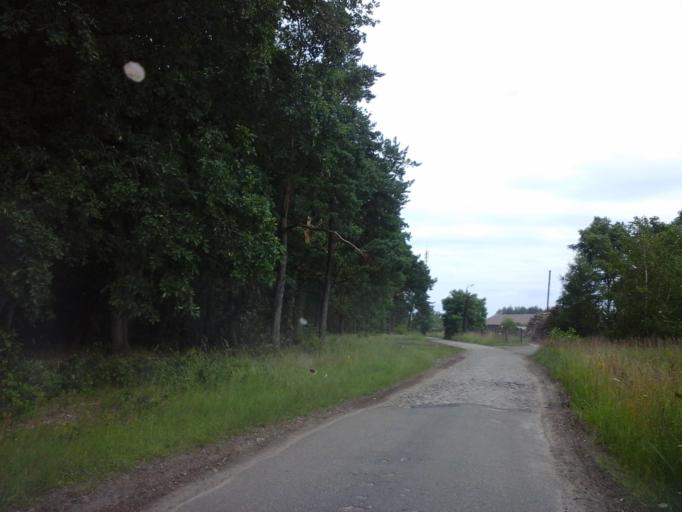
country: PL
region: Lubusz
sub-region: Powiat strzelecko-drezdenecki
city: Dobiegniew
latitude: 53.0922
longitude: 15.7895
